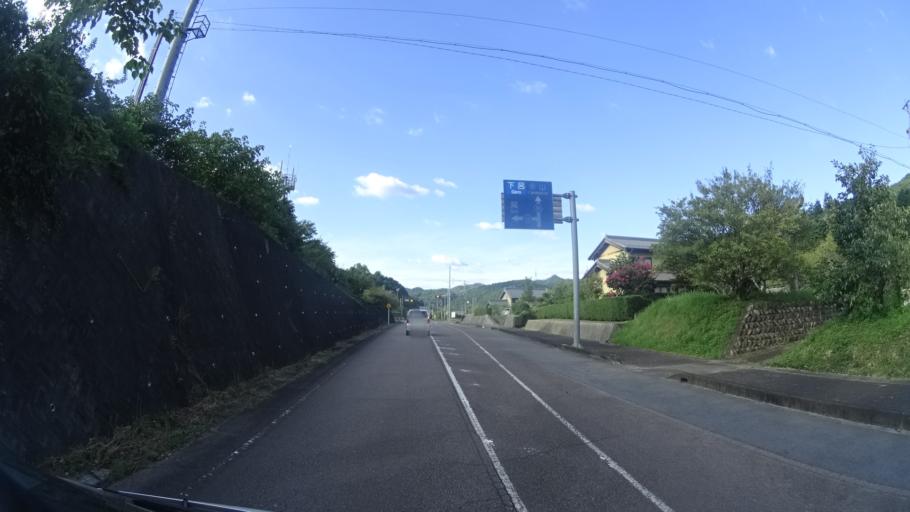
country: JP
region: Gifu
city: Minokamo
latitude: 35.5922
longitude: 137.0887
